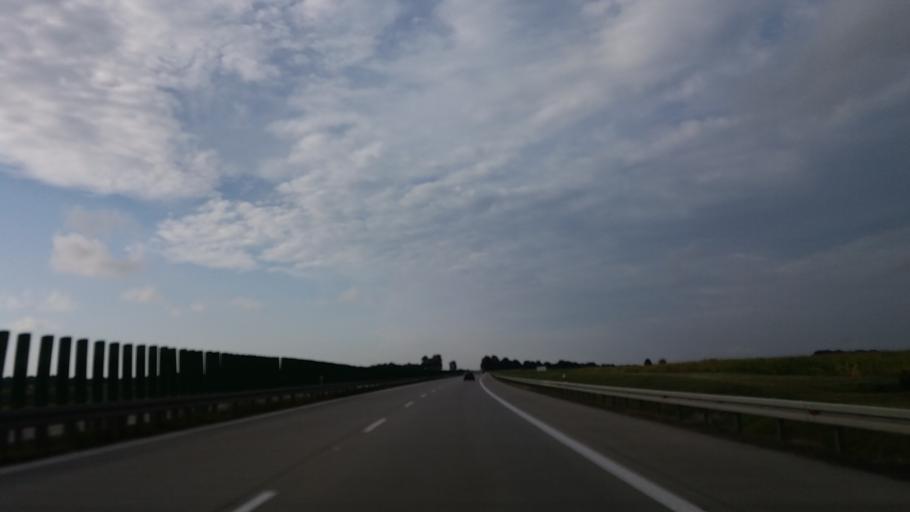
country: PL
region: Lower Silesian Voivodeship
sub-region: Powiat sredzki
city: Udanin
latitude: 51.0953
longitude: 16.4079
